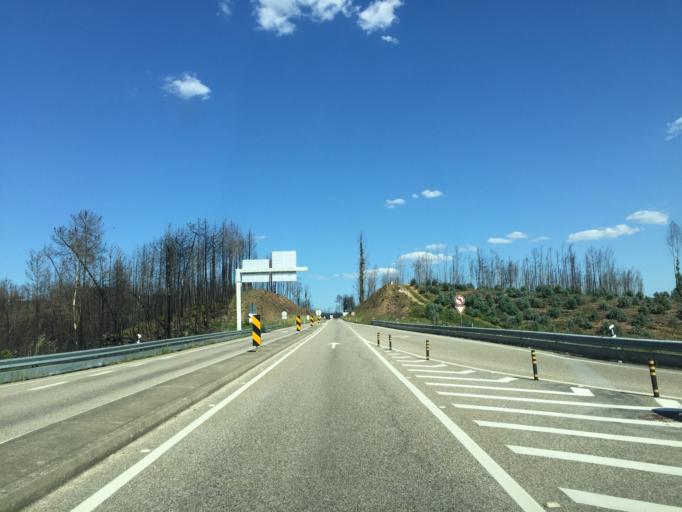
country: PT
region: Leiria
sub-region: Pedrogao Grande
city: Pedrogao Grande
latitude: 39.9274
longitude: -8.1804
